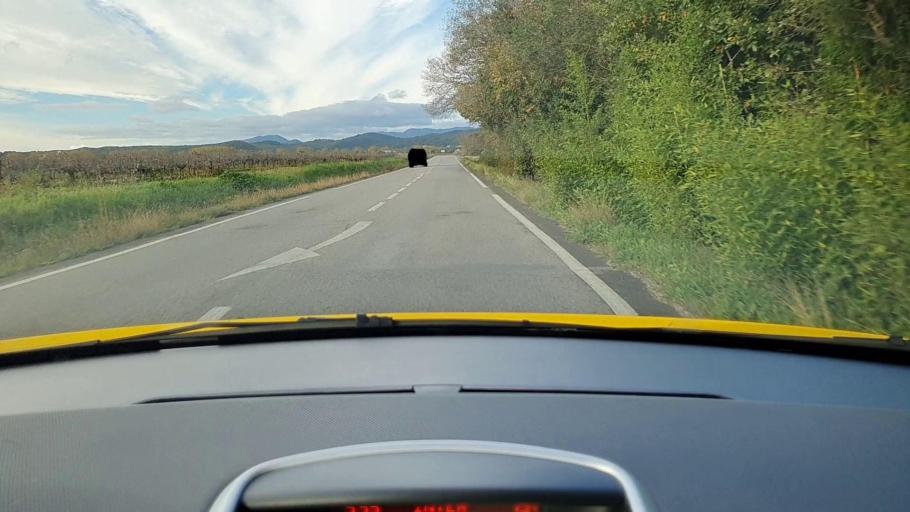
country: FR
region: Languedoc-Roussillon
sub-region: Departement du Gard
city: Lezan
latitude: 44.0217
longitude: 4.0454
